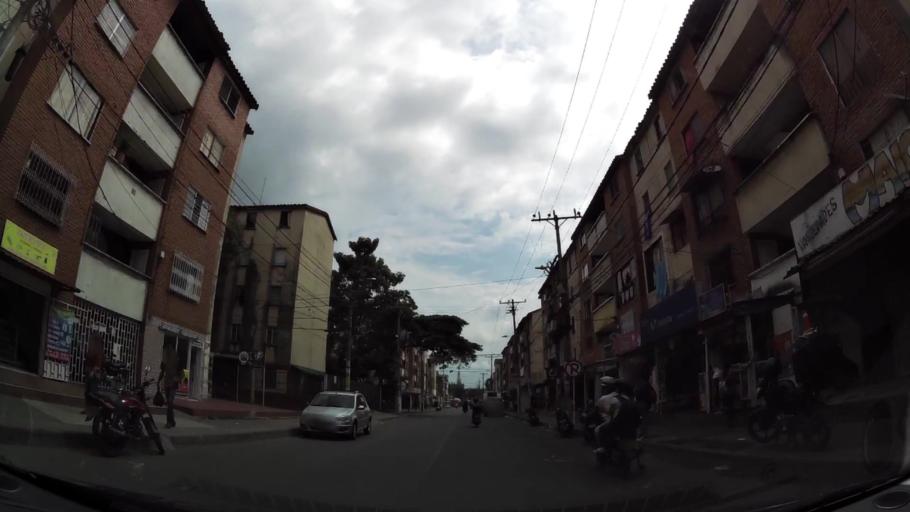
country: CO
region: Valle del Cauca
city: Cali
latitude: 3.4851
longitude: -76.4899
